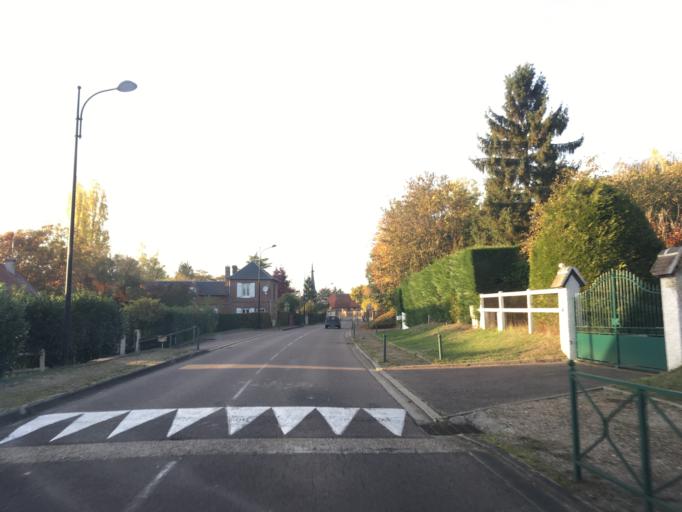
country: FR
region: Haute-Normandie
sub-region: Departement de l'Eure
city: Heudreville-sur-Eure
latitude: 49.1278
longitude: 1.2141
